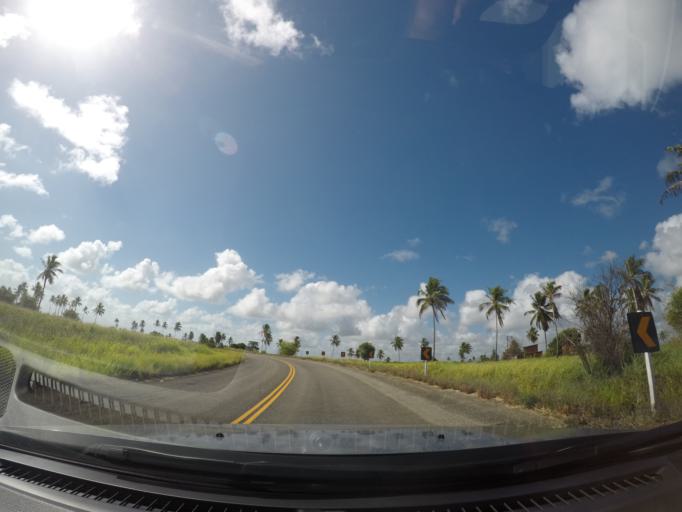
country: BR
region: Paraiba
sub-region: Pitimbu
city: Pitimbu
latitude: -7.3813
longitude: -34.8300
